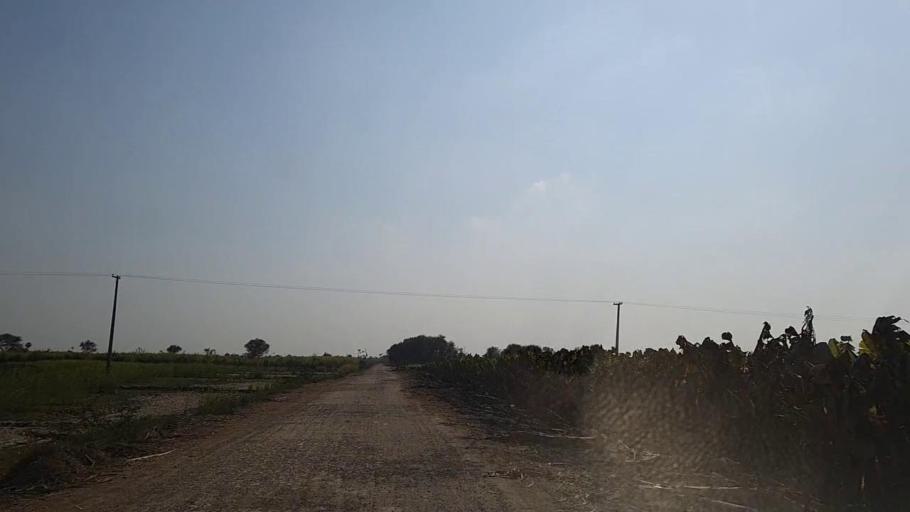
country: PK
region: Sindh
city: Daur
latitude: 26.4210
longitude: 68.2368
